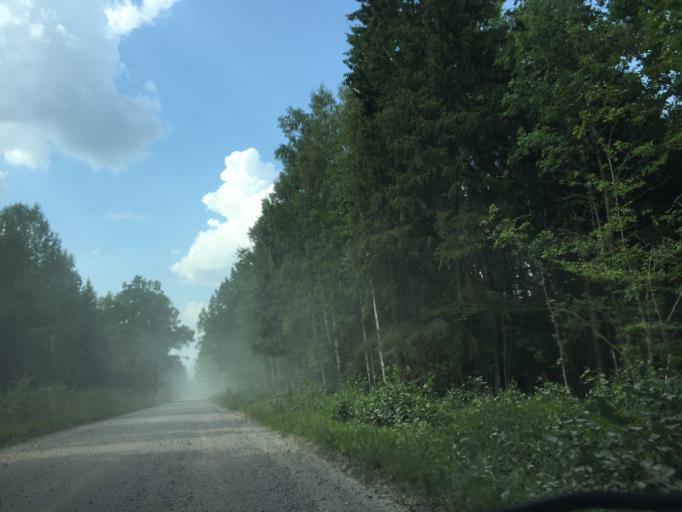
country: LV
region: Auces Novads
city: Auce
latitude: 56.4212
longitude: 22.9752
